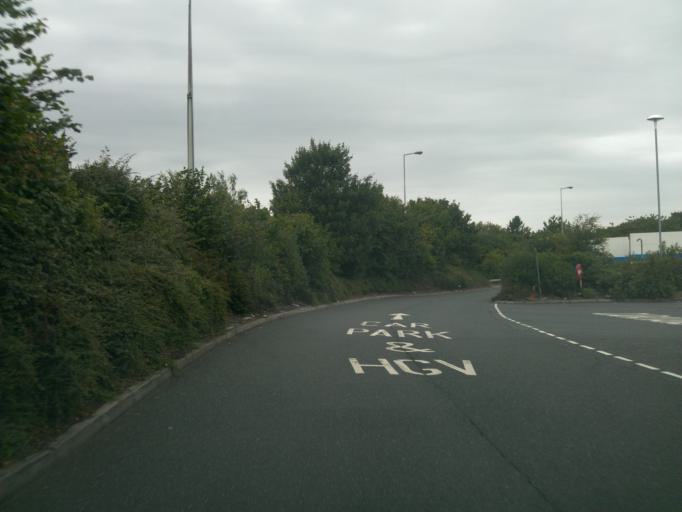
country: GB
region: England
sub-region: Kent
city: West Thurrock
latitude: 51.4930
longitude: 0.2697
